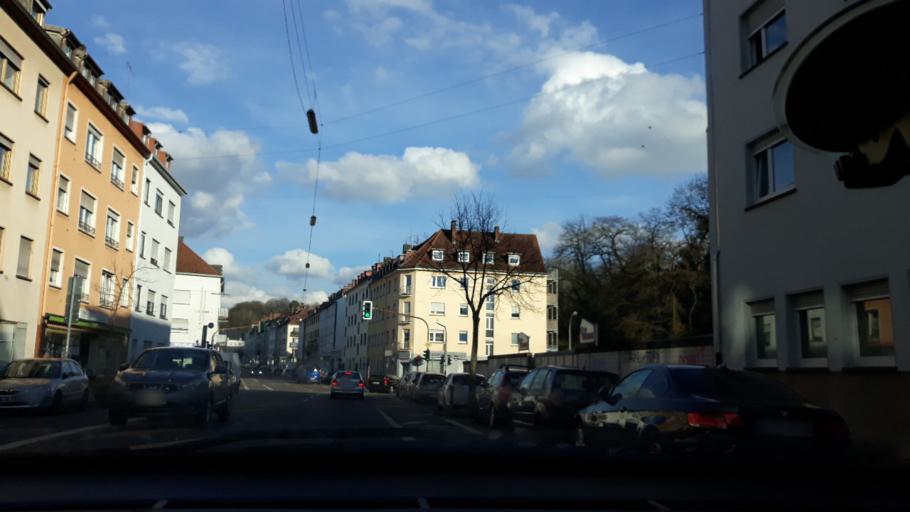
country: DE
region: Saarland
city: Saarbrucken
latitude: 49.2323
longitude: 6.9747
